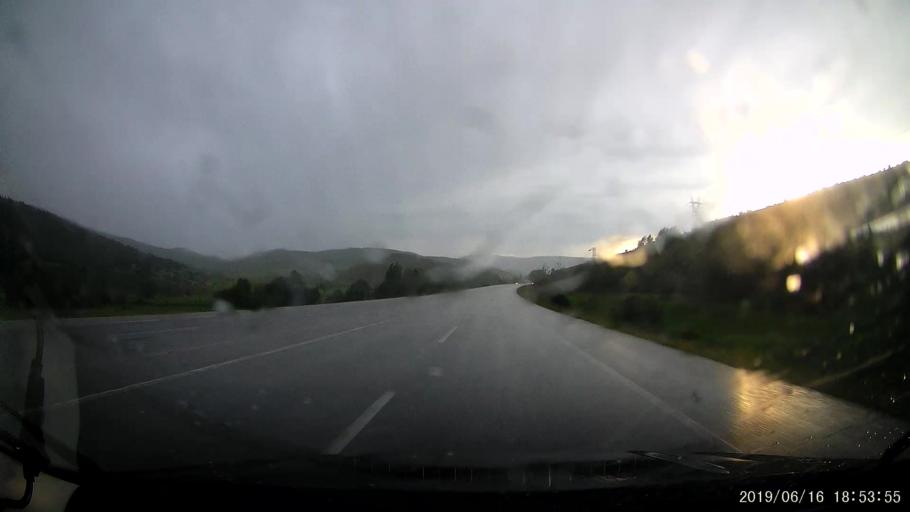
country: TR
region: Erzincan
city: Catalcam
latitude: 39.8966
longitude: 38.8660
